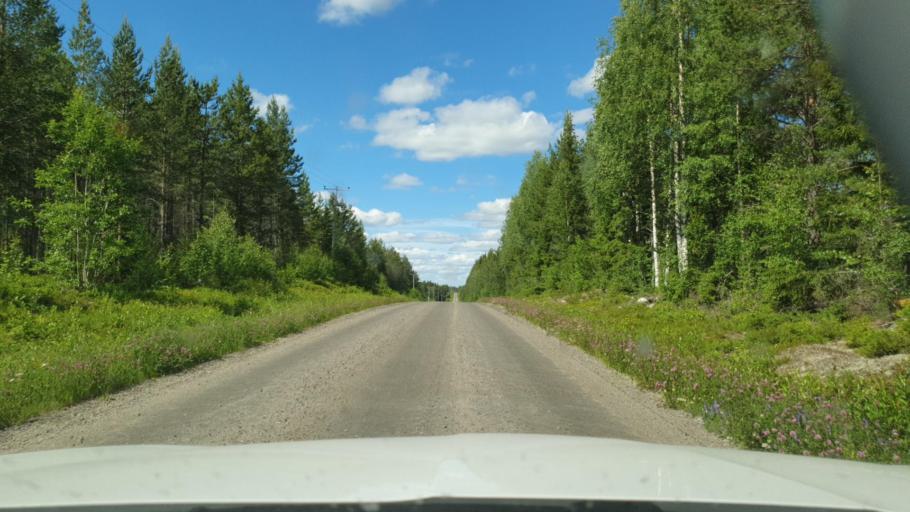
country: SE
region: Vaesterbotten
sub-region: Skelleftea Kommun
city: Backa
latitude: 65.1688
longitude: 21.1186
